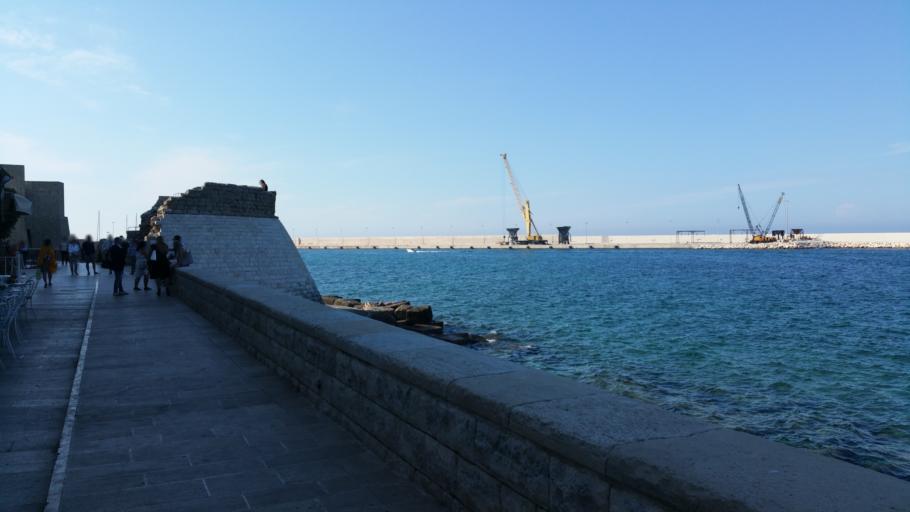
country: IT
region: Apulia
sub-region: Provincia di Bari
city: Monopoli
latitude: 40.9532
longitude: 17.3064
